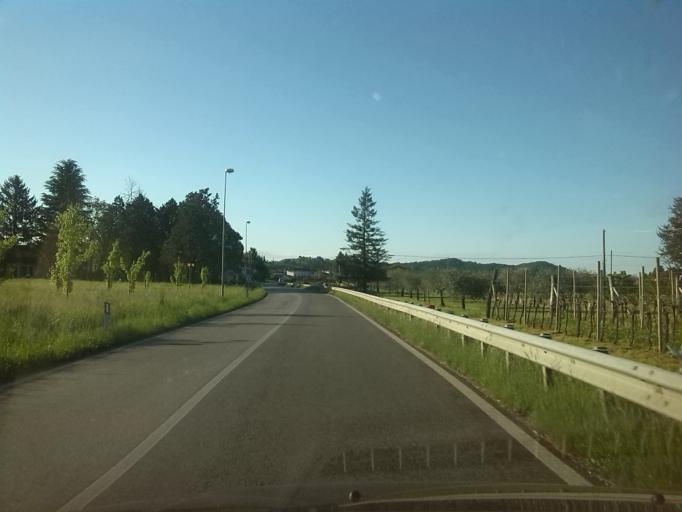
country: IT
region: Friuli Venezia Giulia
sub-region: Provincia di Gorizia
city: Dolegna del Collio
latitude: 46.0386
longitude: 13.4397
